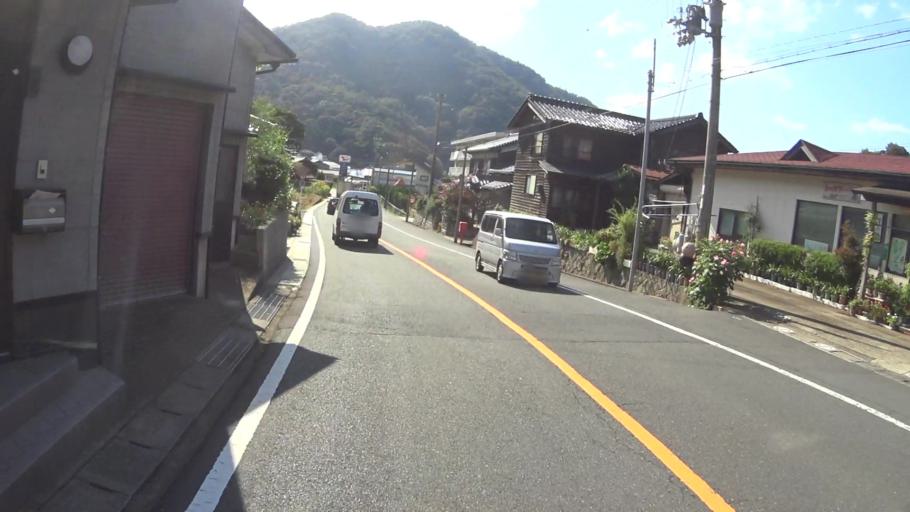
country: JP
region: Kyoto
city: Miyazu
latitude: 35.7491
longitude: 135.1673
